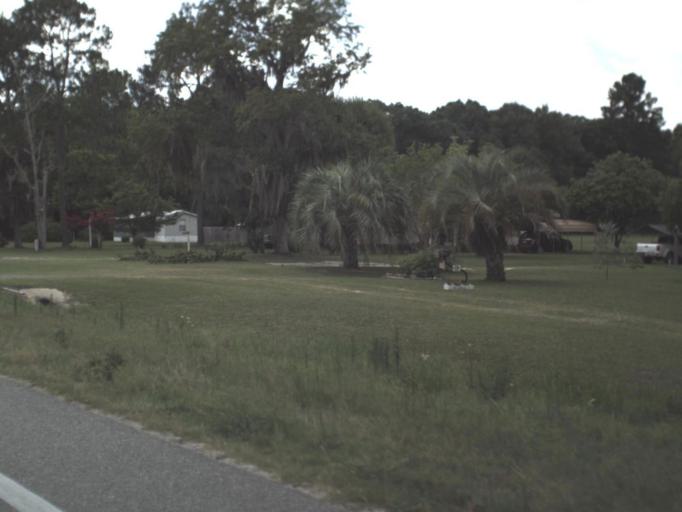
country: US
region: Florida
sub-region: Hamilton County
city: Jasper
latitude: 30.5241
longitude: -83.0043
